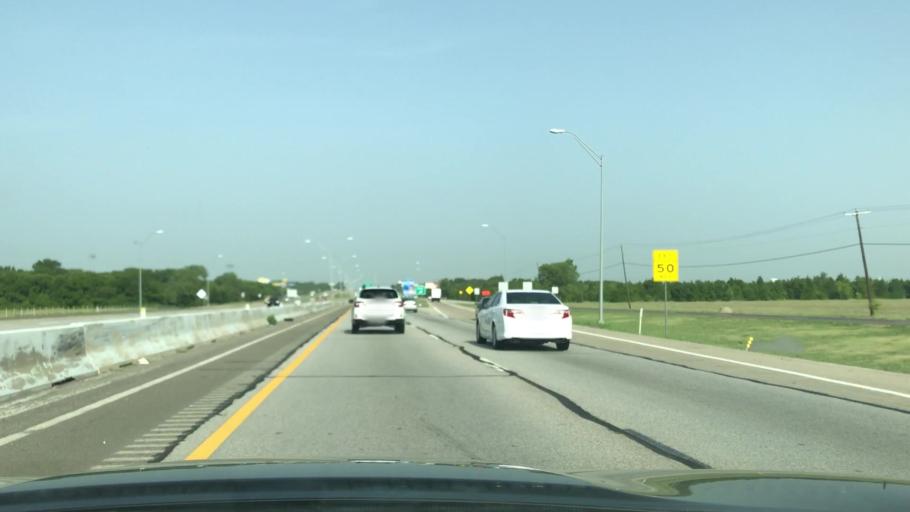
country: US
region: Texas
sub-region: Dallas County
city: Mesquite
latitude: 32.7892
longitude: -96.5872
